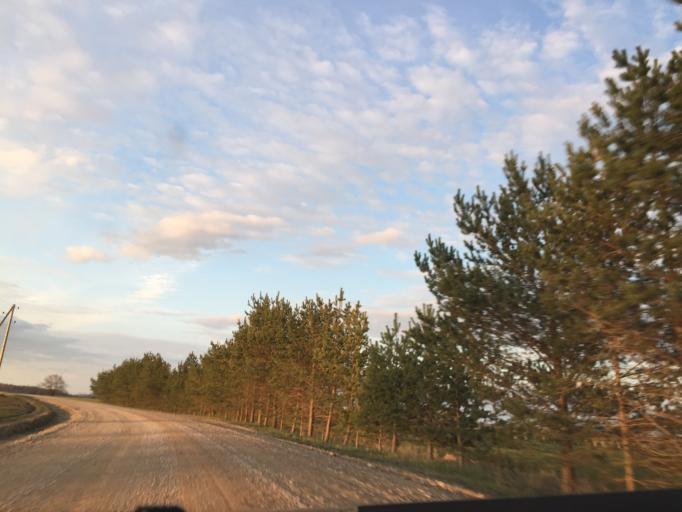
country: LV
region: Gulbenes Rajons
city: Gulbene
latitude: 57.1927
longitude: 26.7586
